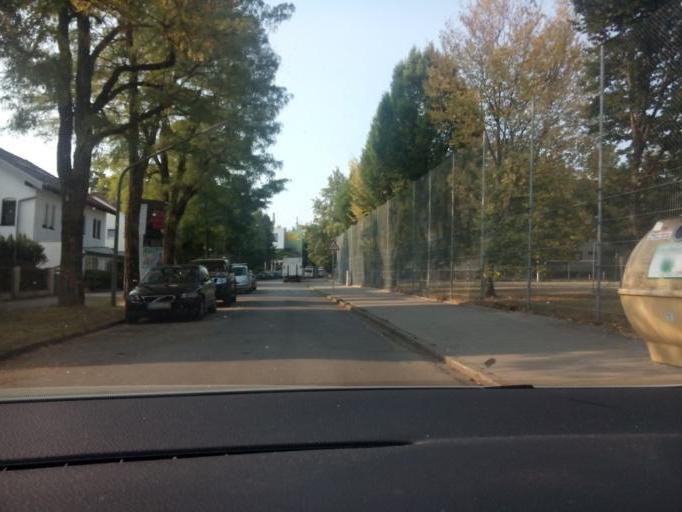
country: DE
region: Bavaria
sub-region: Upper Bavaria
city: Munich
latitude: 48.1135
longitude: 11.5969
